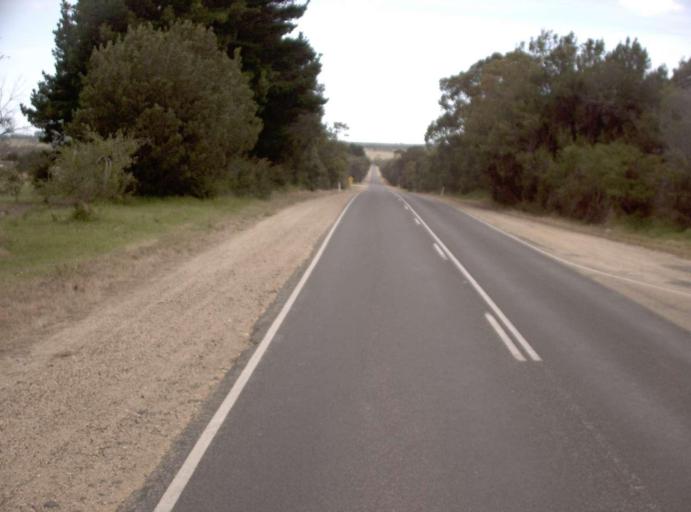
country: AU
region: Victoria
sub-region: Wellington
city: Sale
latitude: -38.1897
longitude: 147.0931
